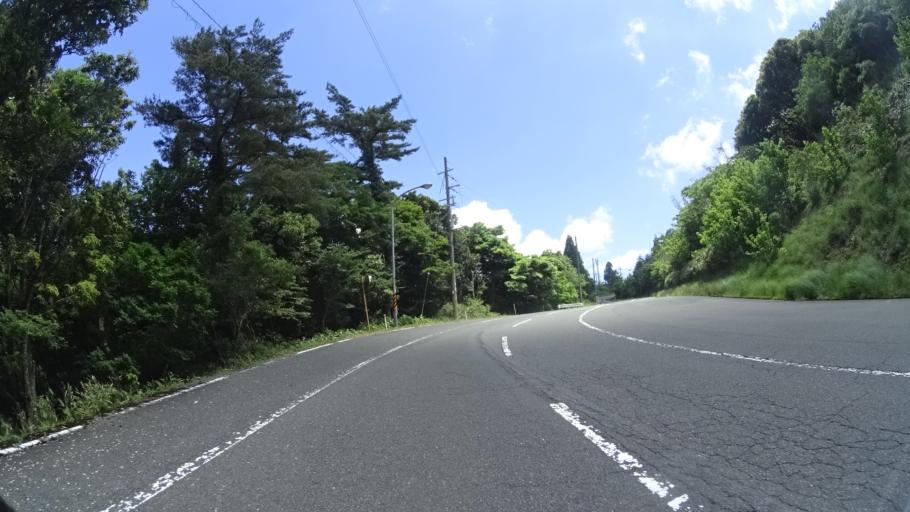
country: JP
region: Kyoto
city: Miyazu
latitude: 35.4787
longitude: 135.1611
